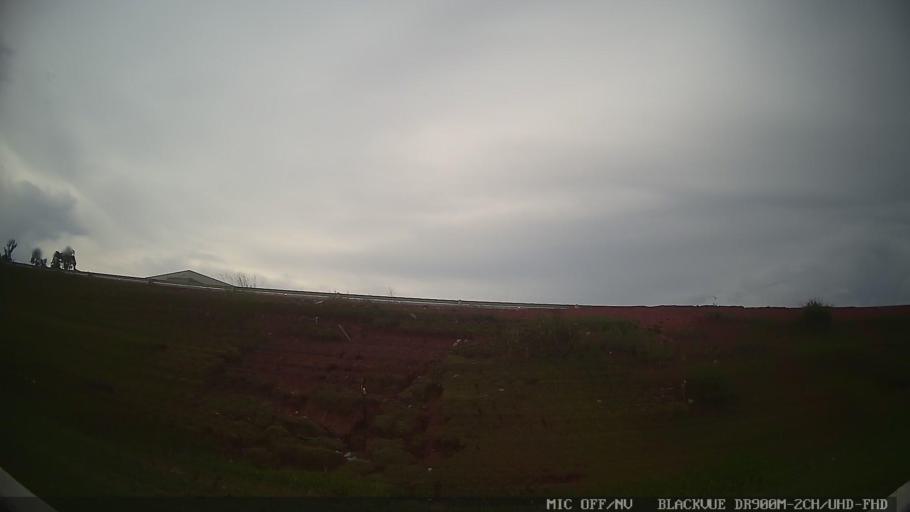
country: BR
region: Sao Paulo
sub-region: Aruja
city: Aruja
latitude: -23.4332
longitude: -46.2699
